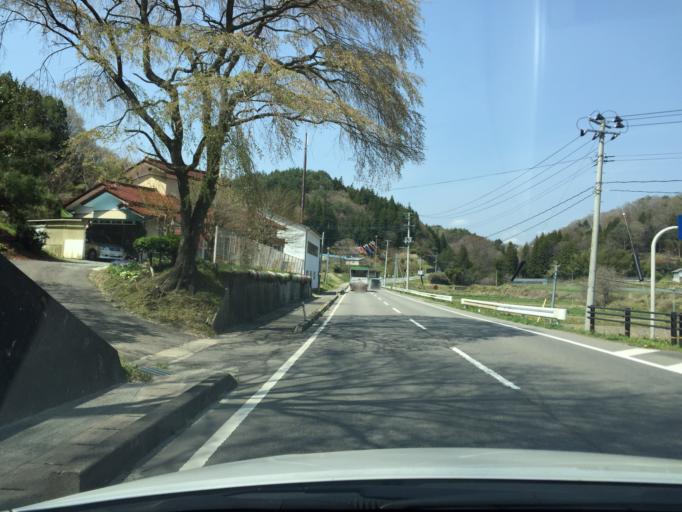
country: JP
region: Fukushima
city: Funehikimachi-funehiki
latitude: 37.4452
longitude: 140.6706
